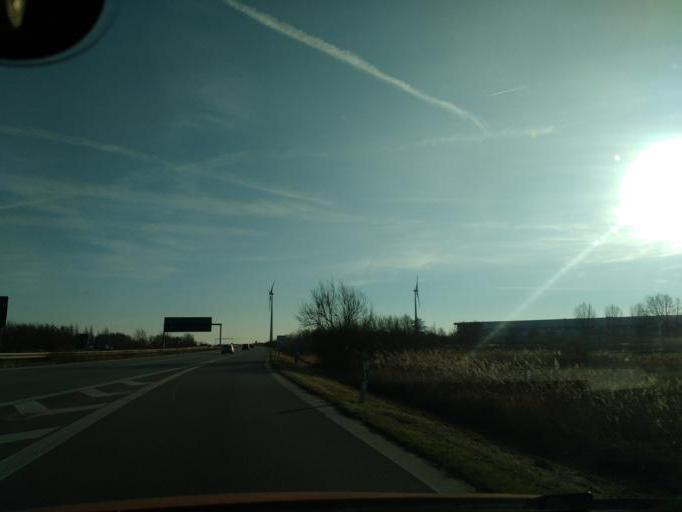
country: DE
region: Berlin
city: Buchholz
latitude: 52.6396
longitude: 13.4325
